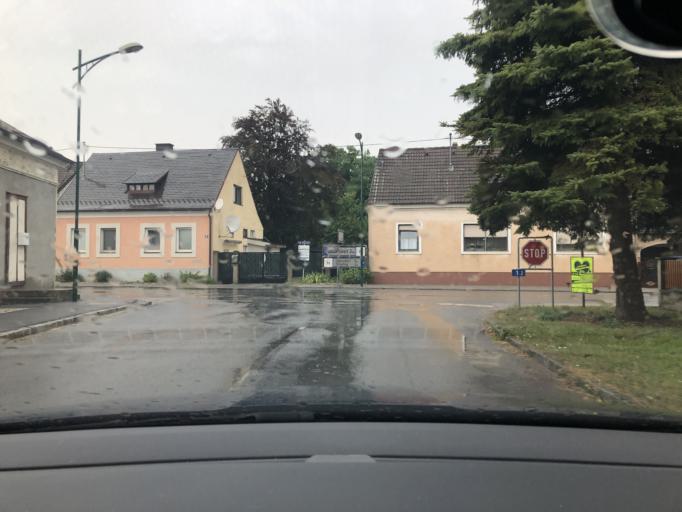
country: AT
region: Lower Austria
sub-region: Politischer Bezirk Ganserndorf
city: Weikendorf
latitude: 48.3439
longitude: 16.7700
